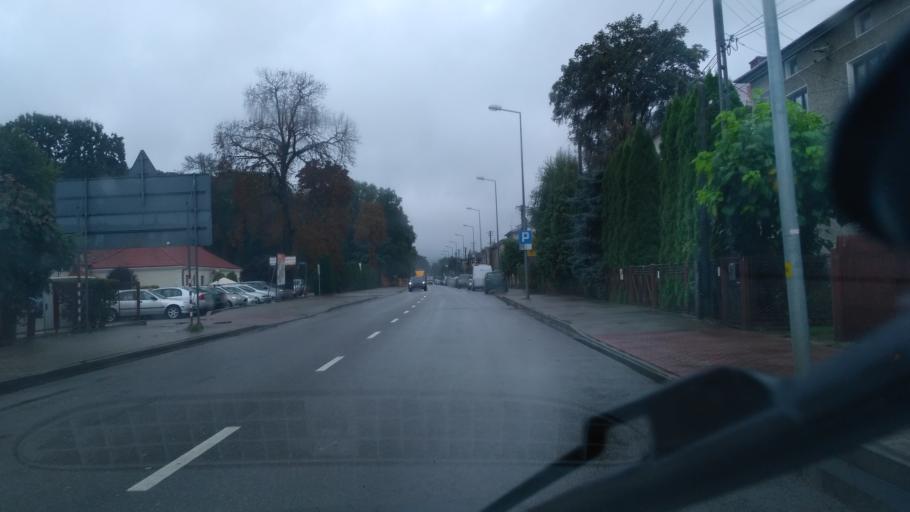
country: PL
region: Subcarpathian Voivodeship
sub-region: Powiat debicki
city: Debica
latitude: 50.0623
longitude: 21.4055
